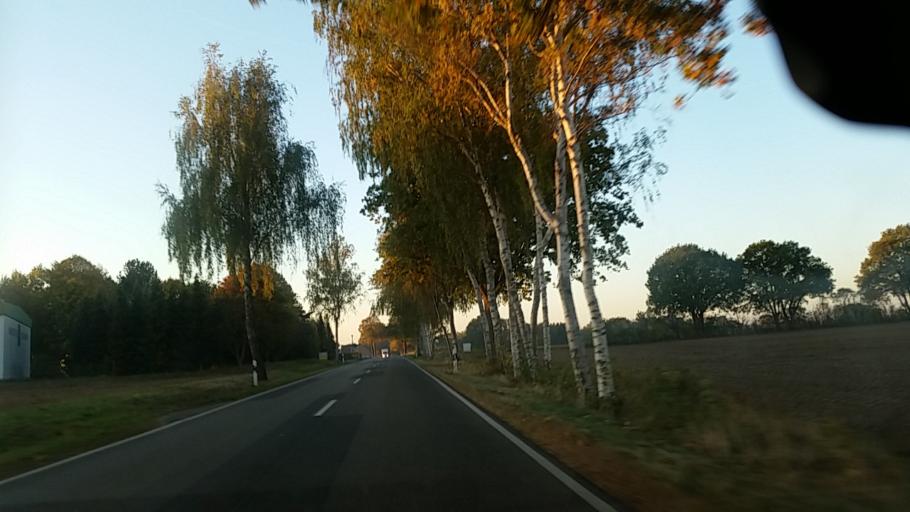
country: DE
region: Lower Saxony
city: Wittingen
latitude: 52.7669
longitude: 10.7106
